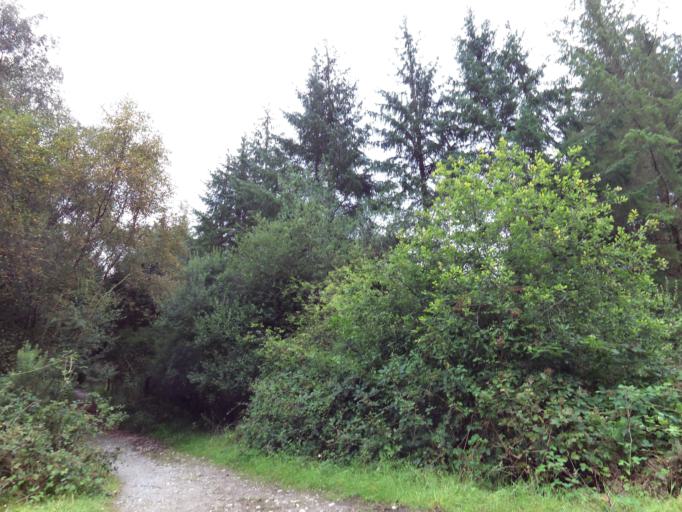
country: IE
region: Connaught
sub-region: County Galway
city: Loughrea
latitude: 53.1298
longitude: -8.4868
